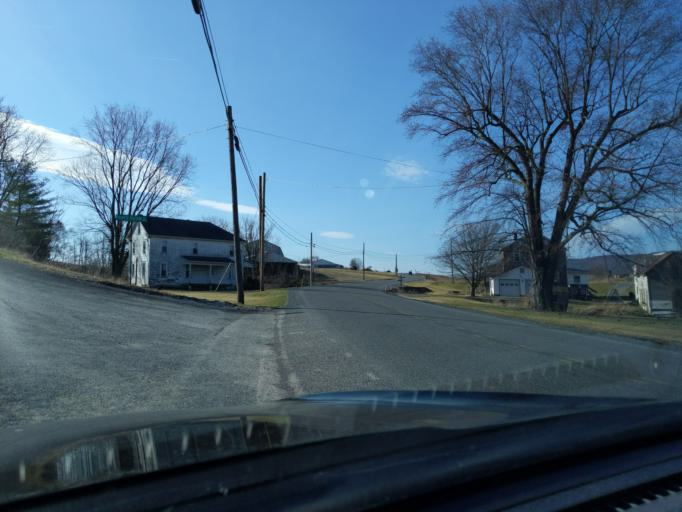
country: US
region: Pennsylvania
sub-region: Blair County
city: Williamsburg
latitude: 40.3999
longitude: -78.2777
